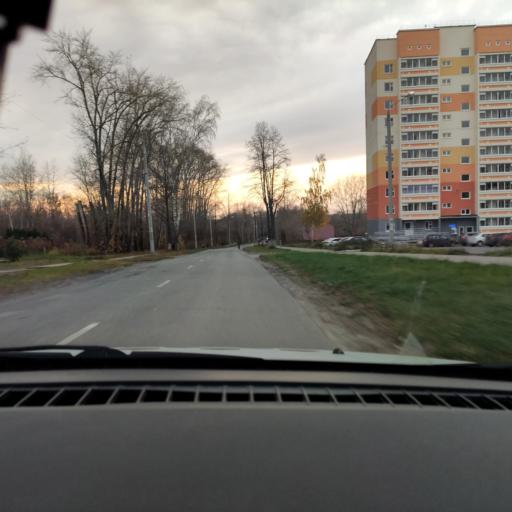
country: RU
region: Perm
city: Perm
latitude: 58.1206
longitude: 56.3798
